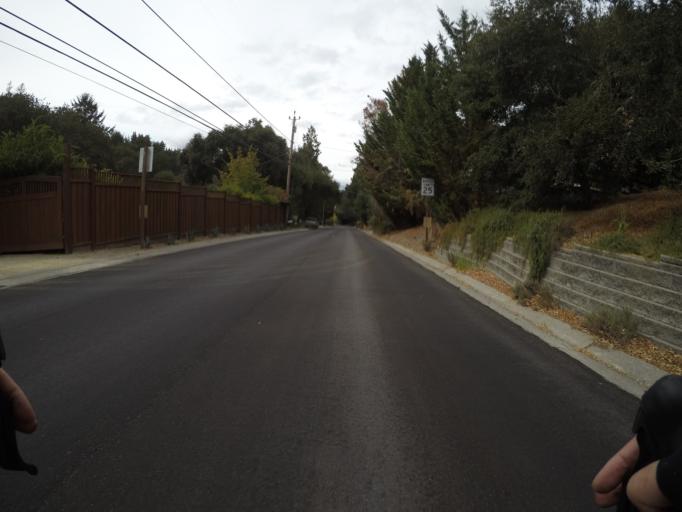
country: US
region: California
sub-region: Santa Cruz County
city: Felton
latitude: 37.0717
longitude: -122.0726
